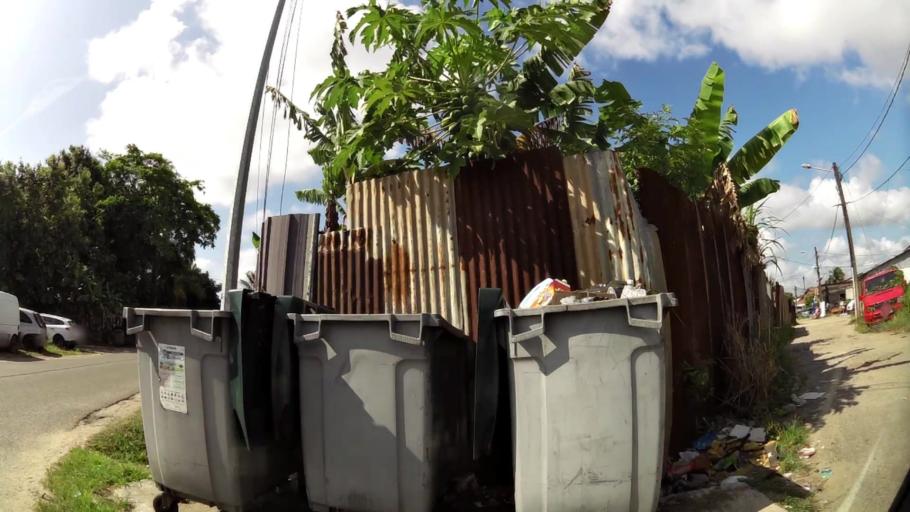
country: GF
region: Guyane
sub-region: Guyane
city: Cayenne
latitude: 4.9349
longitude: -52.3142
